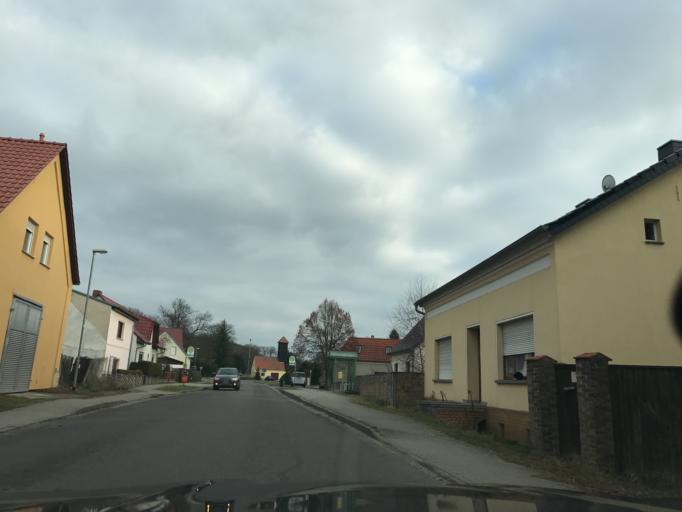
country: DE
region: Brandenburg
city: Brandenburg an der Havel
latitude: 52.3360
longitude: 12.5469
